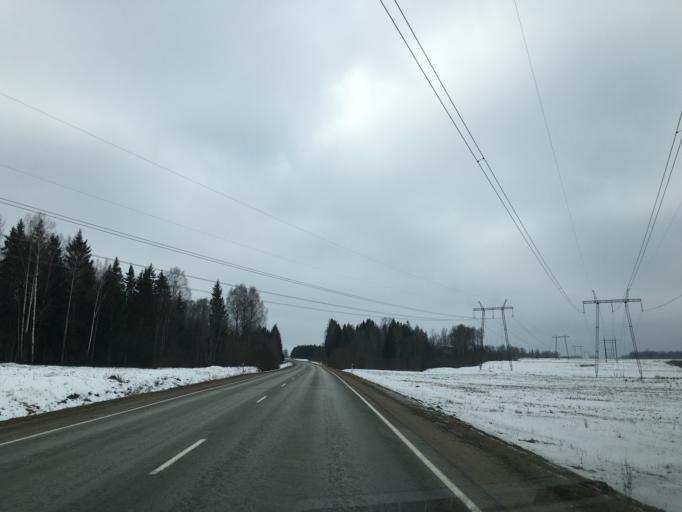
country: EE
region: Tartu
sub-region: Elva linn
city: Elva
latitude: 58.1337
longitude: 26.2455
